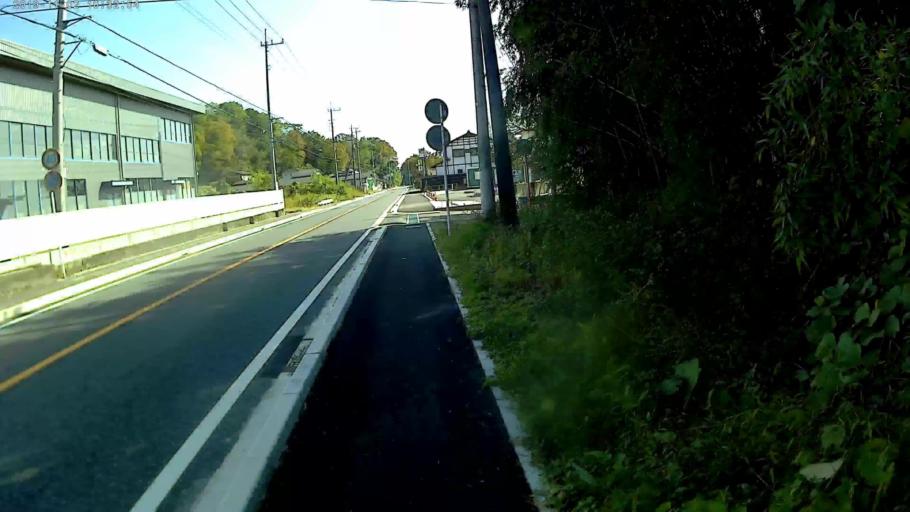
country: JP
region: Gunma
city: Annaka
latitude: 36.3108
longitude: 138.8104
